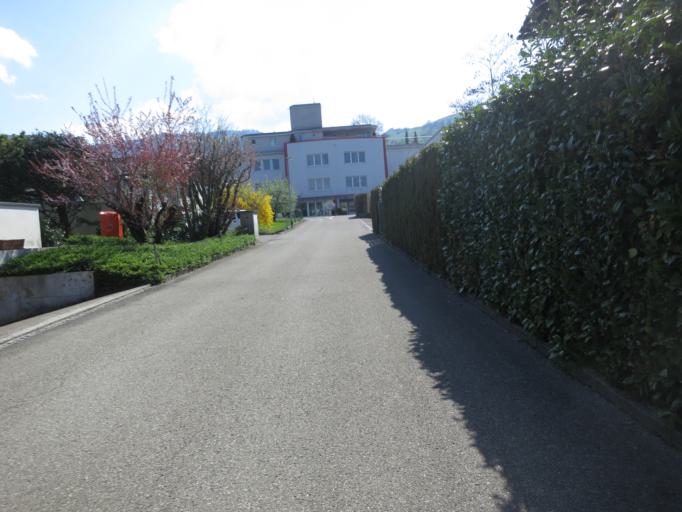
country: CH
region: Schwyz
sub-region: Bezirk March
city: Lachen
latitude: 47.1872
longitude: 8.8517
